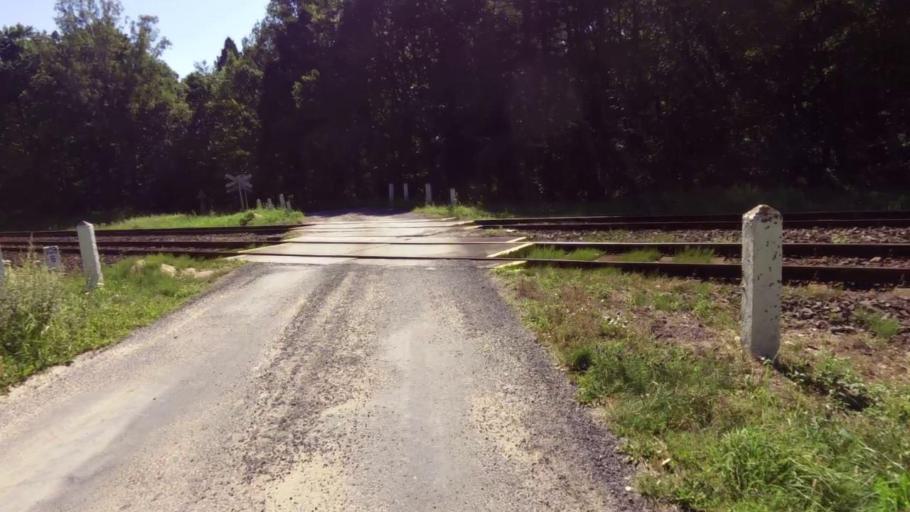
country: PL
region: West Pomeranian Voivodeship
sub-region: Powiat drawski
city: Wierzchowo
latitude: 53.5277
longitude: 16.0961
